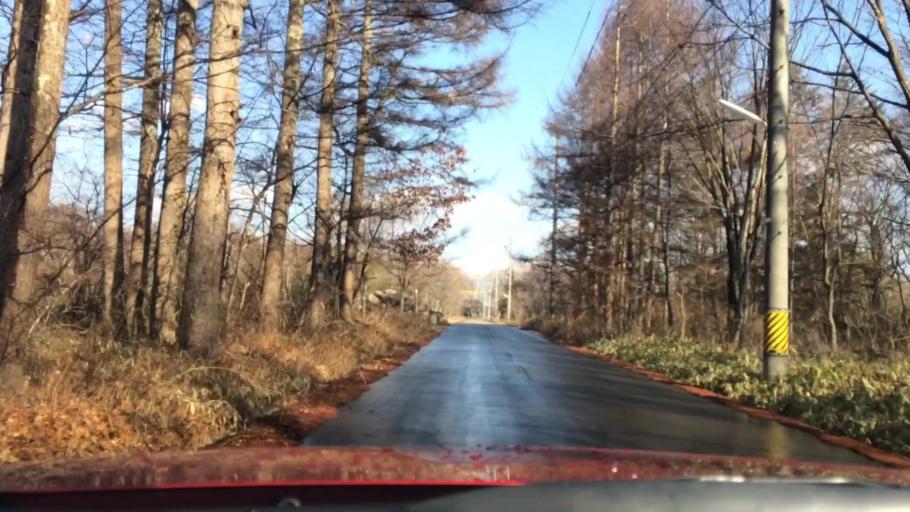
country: JP
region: Nagano
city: Komoro
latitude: 36.3204
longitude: 138.5512
